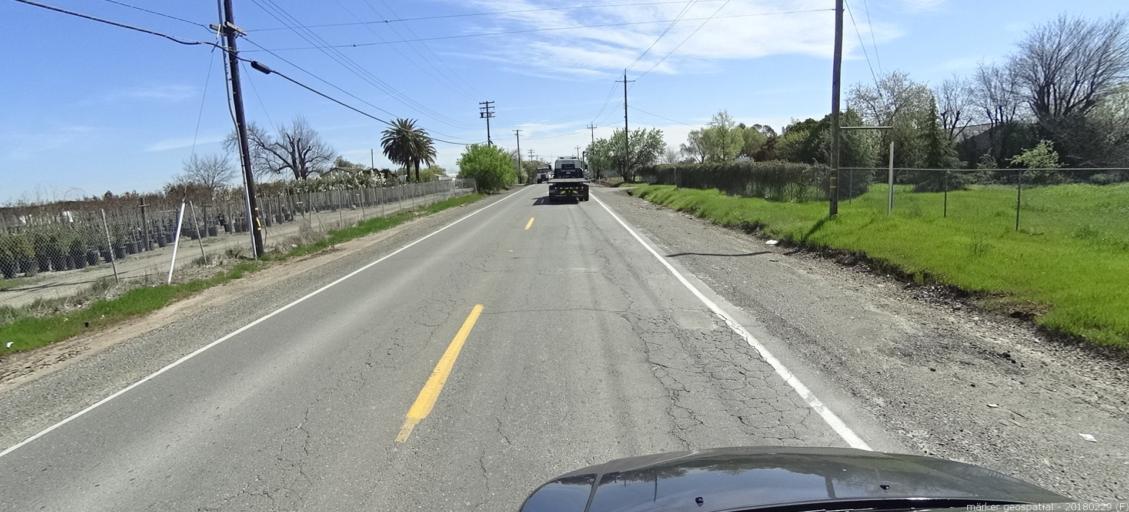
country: US
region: California
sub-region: Sacramento County
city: Rosemont
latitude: 38.5107
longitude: -121.3677
